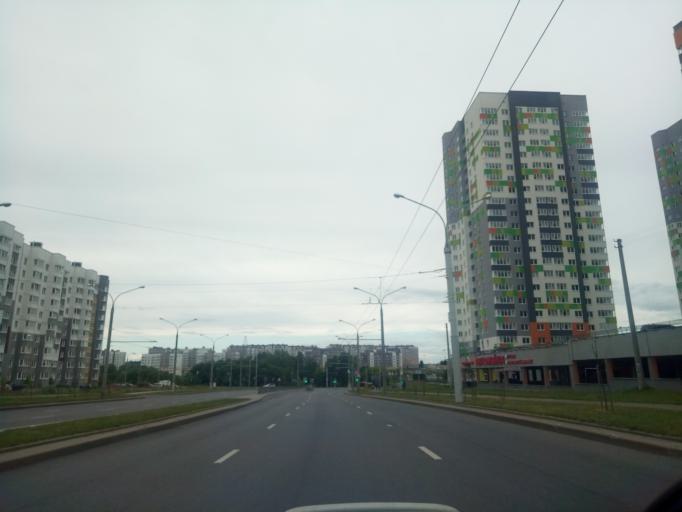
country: BY
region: Minsk
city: Novoye Medvezhino
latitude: 53.8729
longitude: 27.4768
